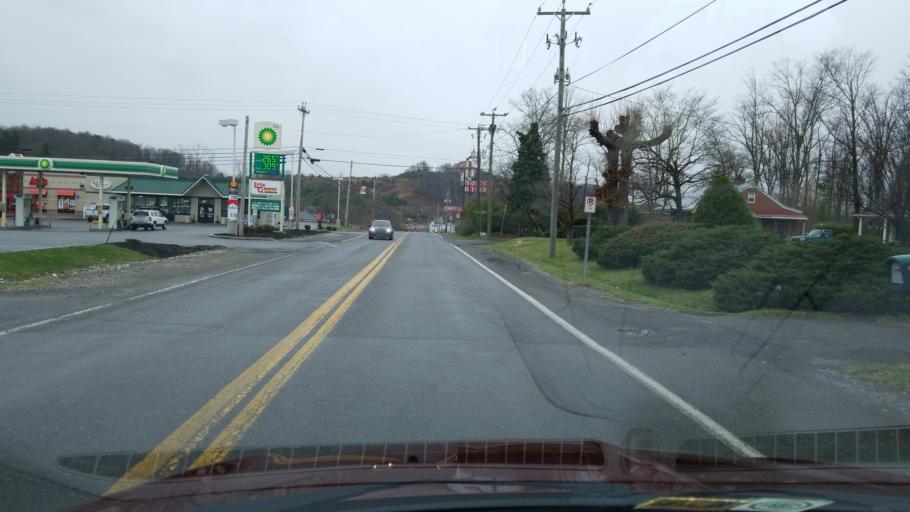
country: US
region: West Virginia
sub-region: Mercer County
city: Princeton
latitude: 37.3644
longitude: -81.0525
